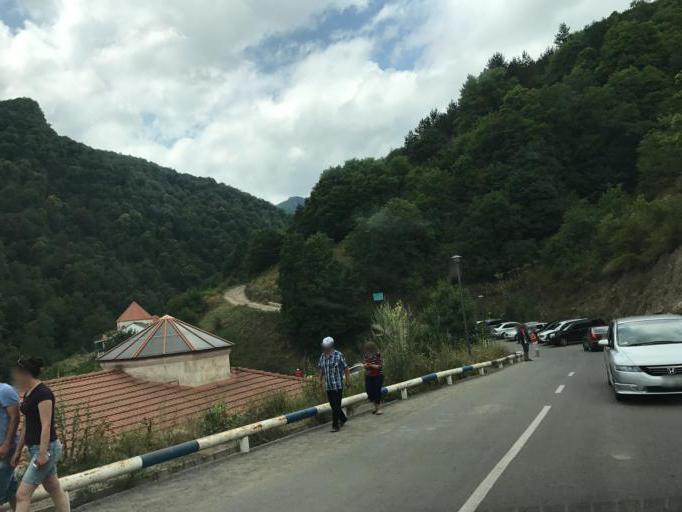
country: AM
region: Tavush
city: Dilijan
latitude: 40.8022
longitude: 44.8908
